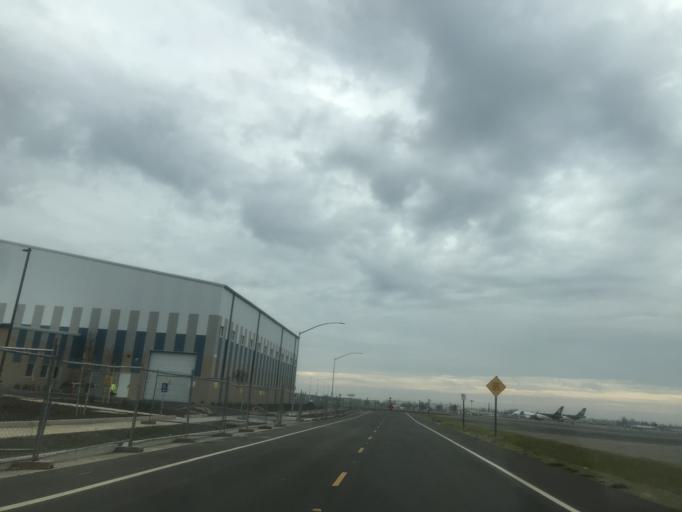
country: US
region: California
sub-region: Sacramento County
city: Rancho Cordova
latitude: 38.5633
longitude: -121.3003
